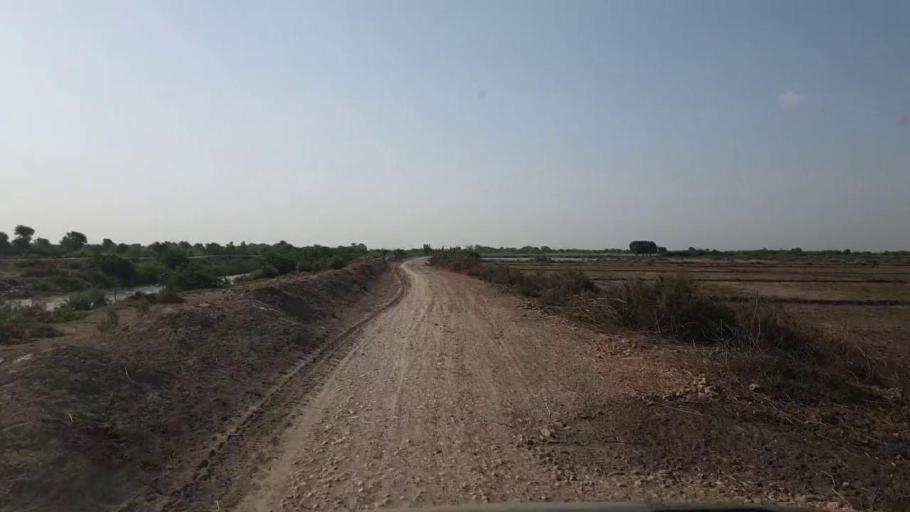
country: PK
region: Sindh
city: Kadhan
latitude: 24.6256
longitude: 69.0733
